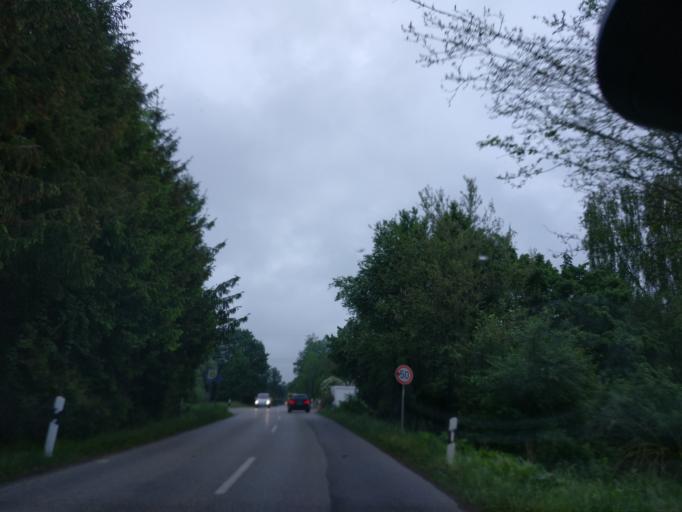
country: DE
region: Bavaria
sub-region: Upper Bavaria
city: Grobenzell
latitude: 48.2032
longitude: 11.4044
